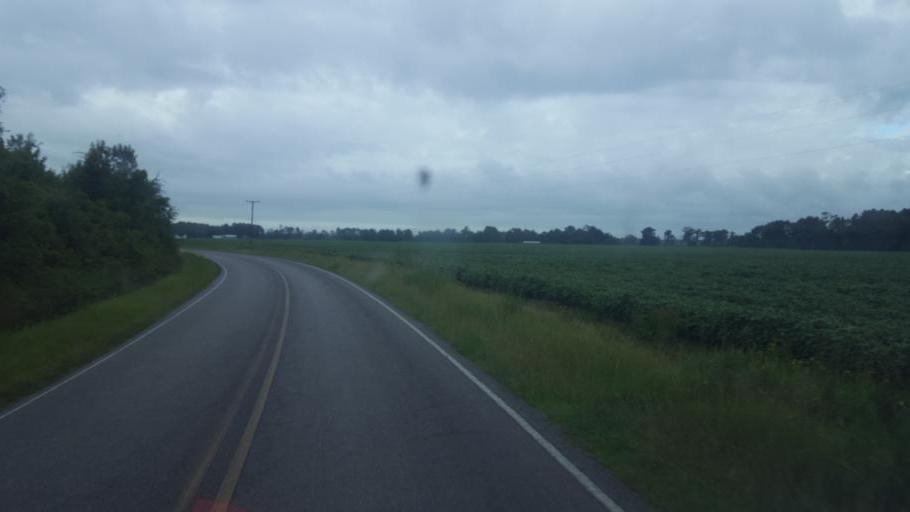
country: US
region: North Carolina
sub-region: Tyrrell County
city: Columbia
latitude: 35.9434
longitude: -76.2821
